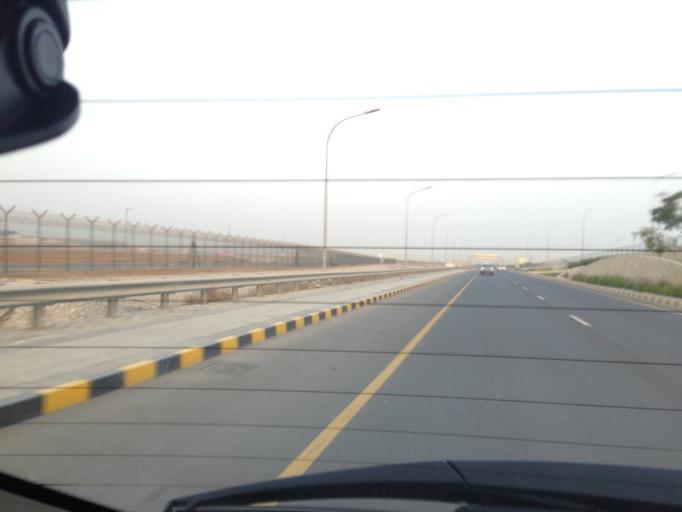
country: OM
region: Muhafazat Masqat
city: Bawshar
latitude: 23.6090
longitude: 58.3081
